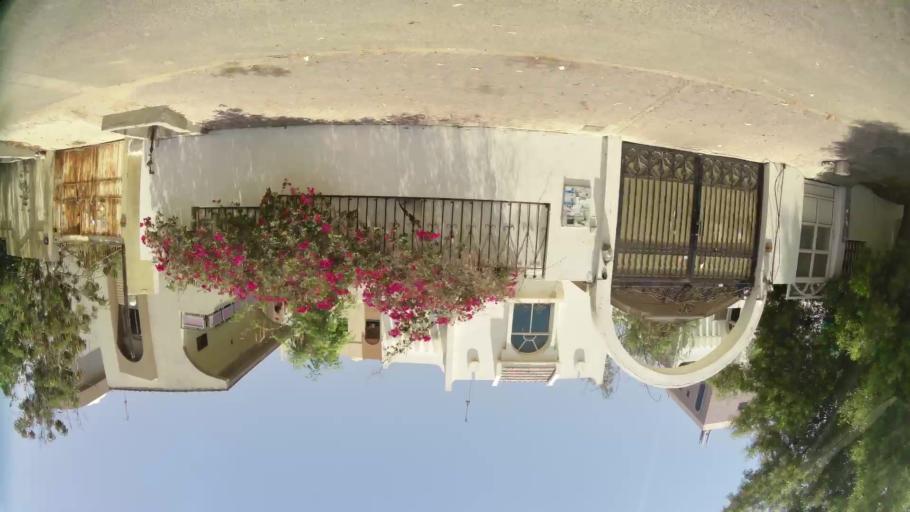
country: AE
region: Ajman
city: Ajman
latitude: 25.4048
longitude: 55.4334
